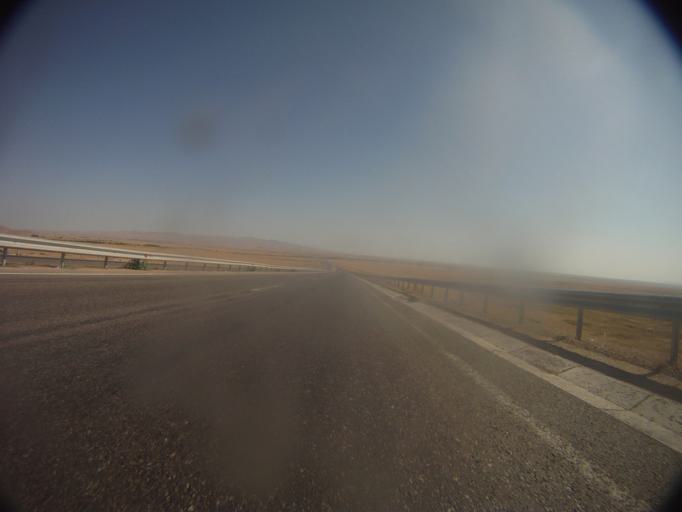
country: KZ
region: Zhambyl
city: Taraz
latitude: 42.7379
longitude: 70.9600
